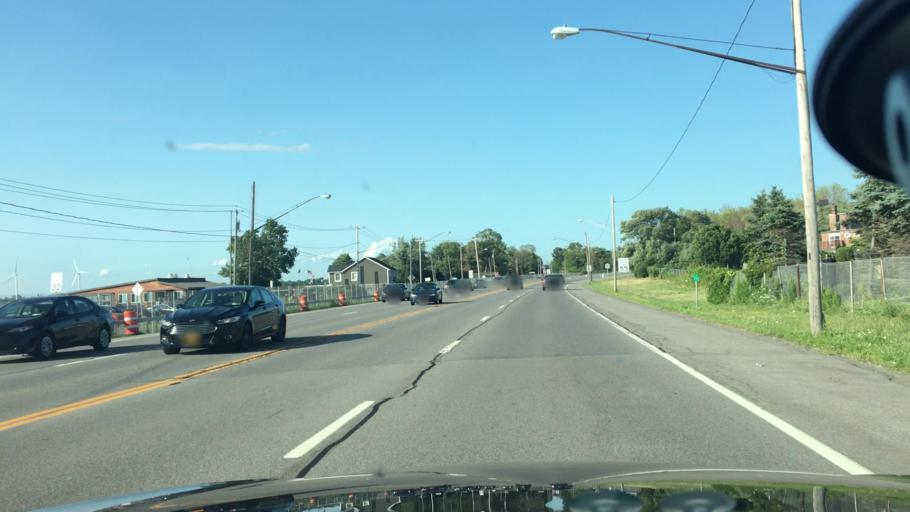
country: US
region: New York
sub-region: Erie County
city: Blasdell
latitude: 42.7742
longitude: -78.8630
